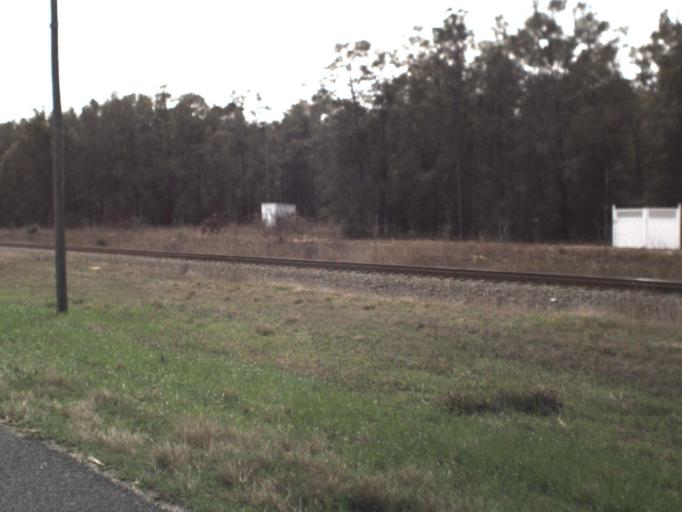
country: US
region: Florida
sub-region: Washington County
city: Chipley
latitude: 30.6375
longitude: -85.3996
